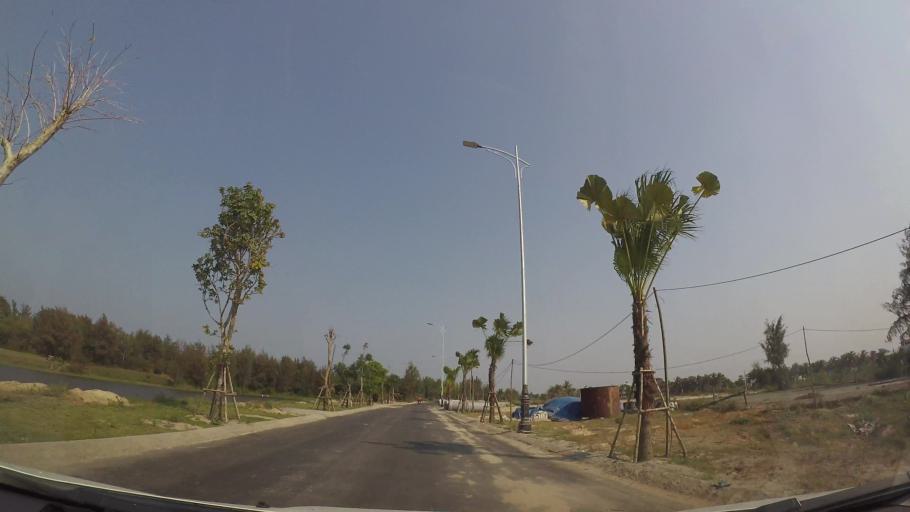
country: VN
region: Da Nang
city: Ngu Hanh Son
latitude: 15.9597
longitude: 108.2797
